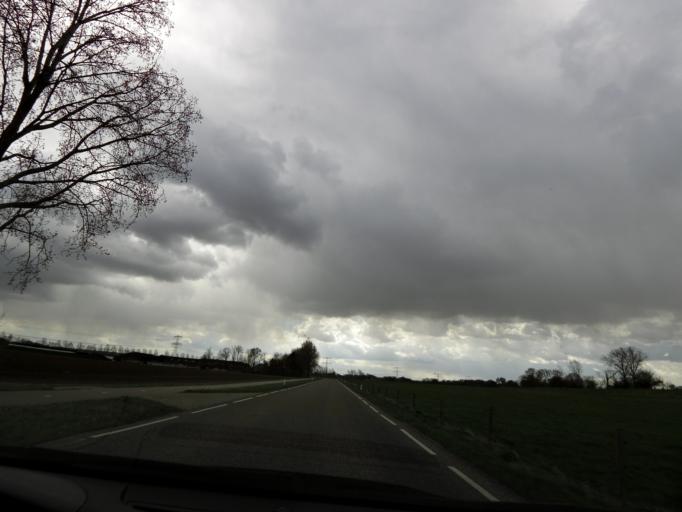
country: BE
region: Flanders
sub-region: Provincie Limburg
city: Maaseik
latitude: 51.0723
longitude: 5.8081
